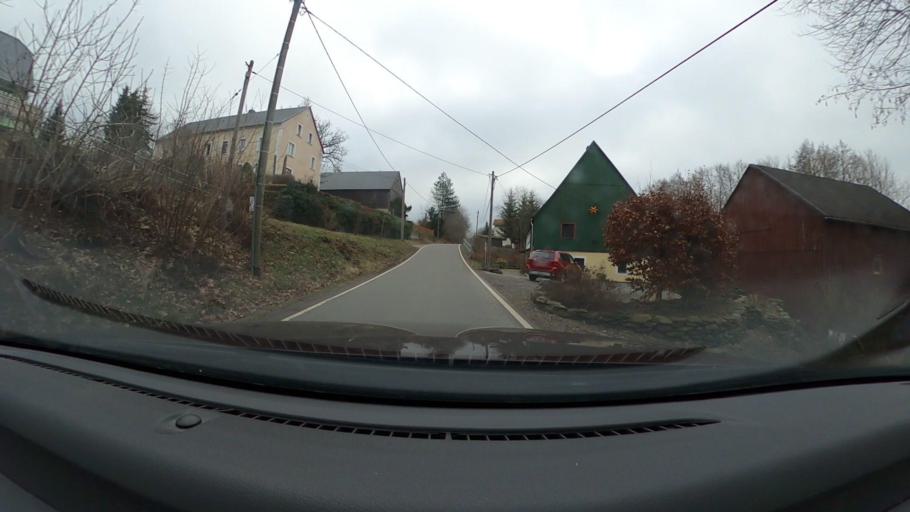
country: DE
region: Saxony
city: Oberschona
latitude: 50.9092
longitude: 13.2767
